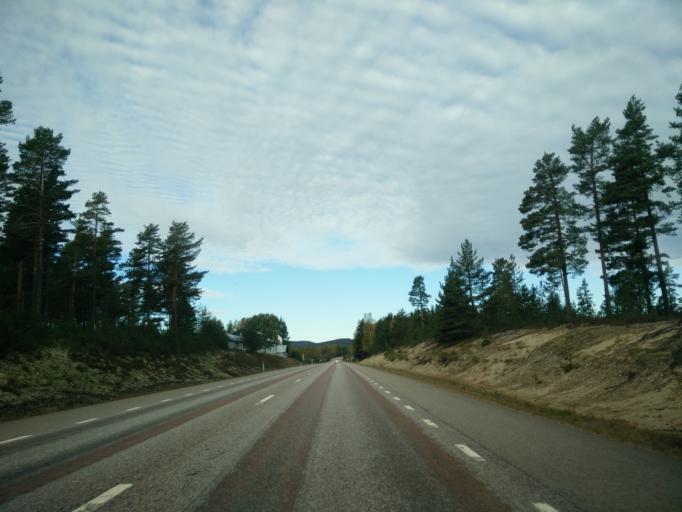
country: SE
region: Gaevleborg
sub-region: Soderhamns Kommun
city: Soderhamn
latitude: 61.2985
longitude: 16.8311
